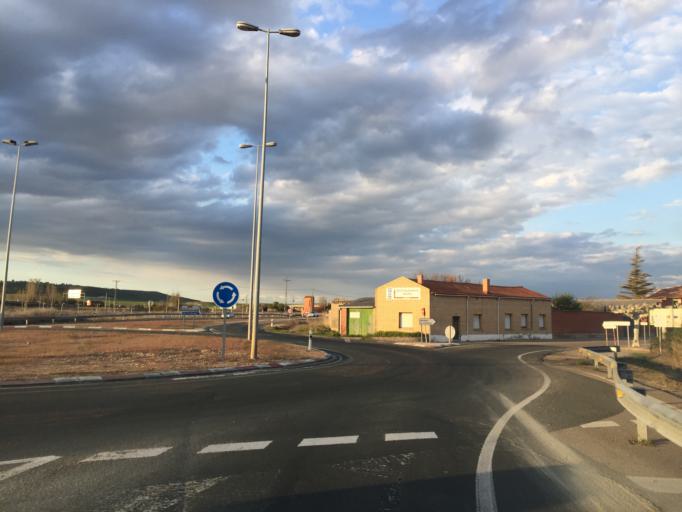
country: ES
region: Castille and Leon
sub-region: Provincia de Palencia
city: Soto de Cerrato
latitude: 41.9814
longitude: -4.4314
